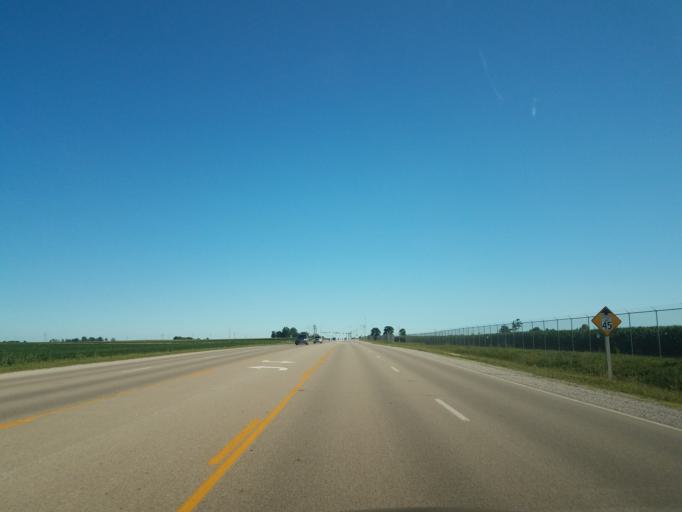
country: US
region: Illinois
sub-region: McLean County
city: Downs
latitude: 40.4774
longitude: -88.9024
